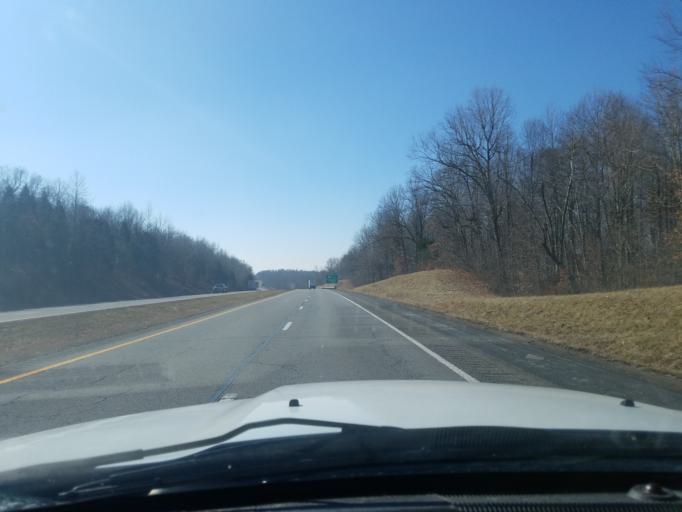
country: US
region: Kentucky
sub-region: Hardin County
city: Elizabethtown
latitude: 37.6724
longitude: -85.8736
